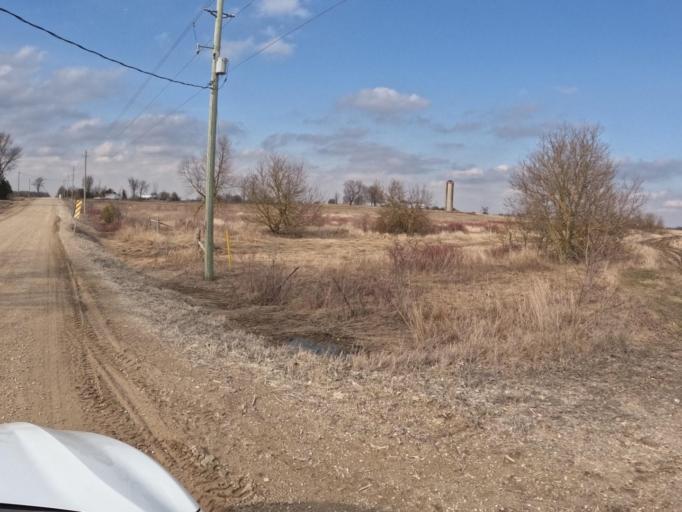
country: CA
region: Ontario
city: Shelburne
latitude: 43.9127
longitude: -80.3042
